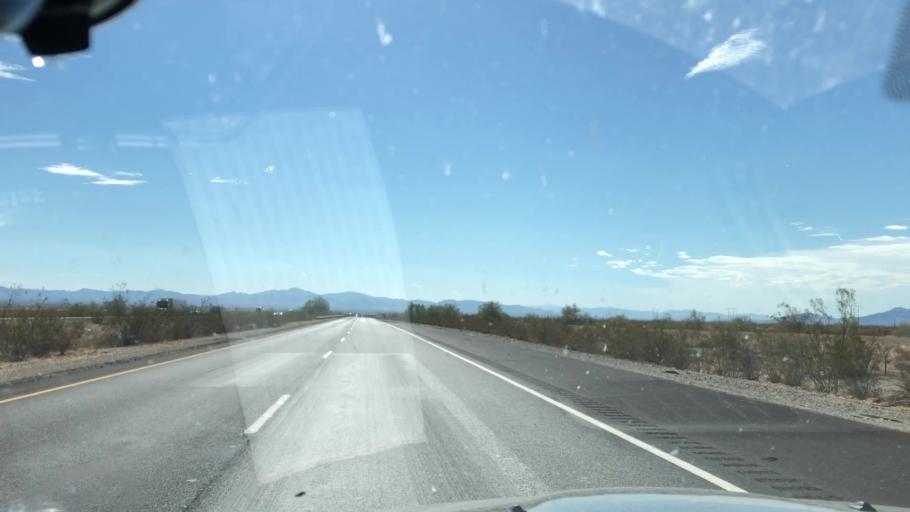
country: US
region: California
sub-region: Riverside County
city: Mesa Verde
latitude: 33.6100
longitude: -114.8418
